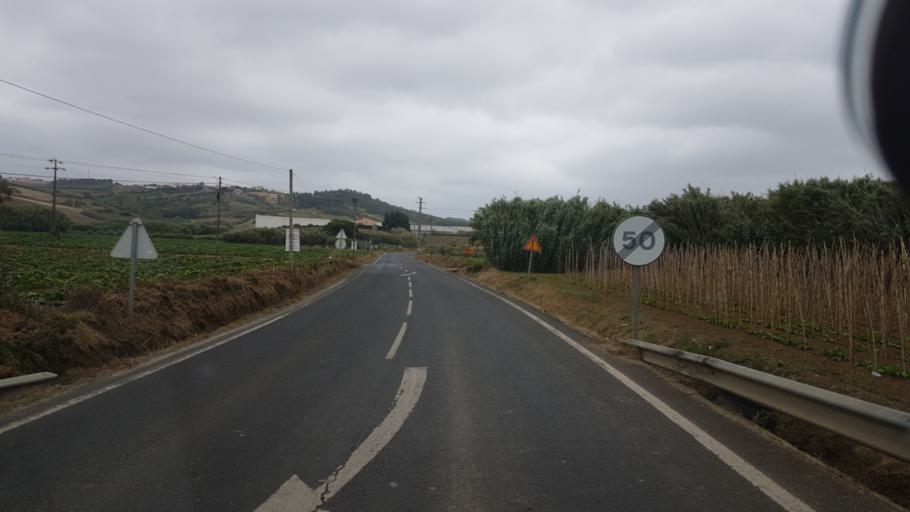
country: PT
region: Lisbon
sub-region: Lourinha
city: Lourinha
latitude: 39.2337
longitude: -9.3137
